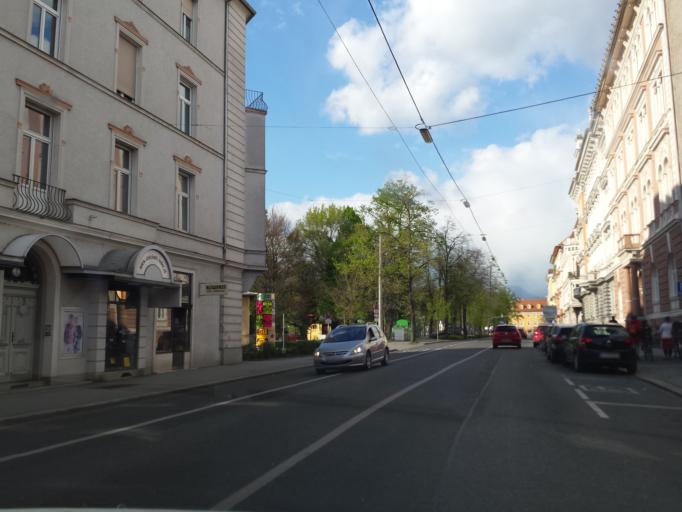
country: AT
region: Styria
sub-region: Graz Stadt
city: Graz
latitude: 47.0721
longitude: 15.4289
